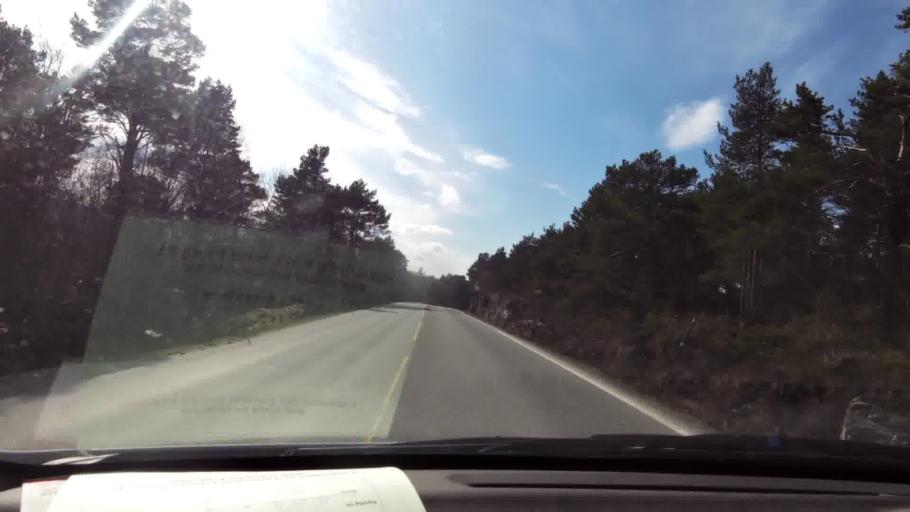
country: NO
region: More og Romsdal
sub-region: Kristiansund
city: Rensvik
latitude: 63.1080
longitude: 7.8327
